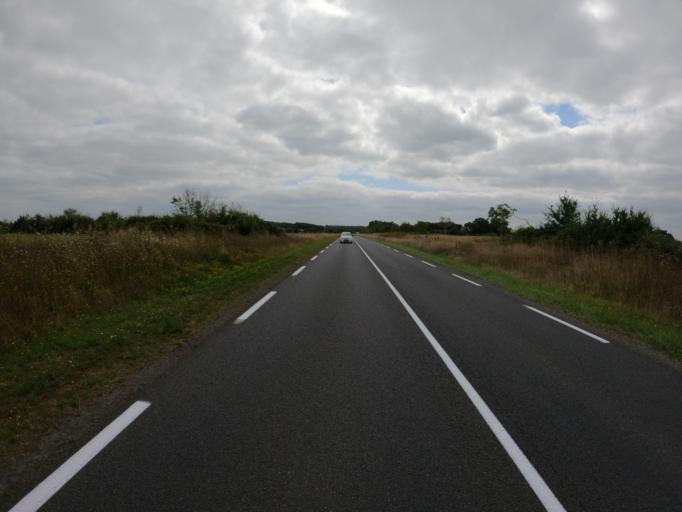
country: FR
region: Poitou-Charentes
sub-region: Departement de la Vienne
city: Charroux
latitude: 46.1450
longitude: 0.4161
